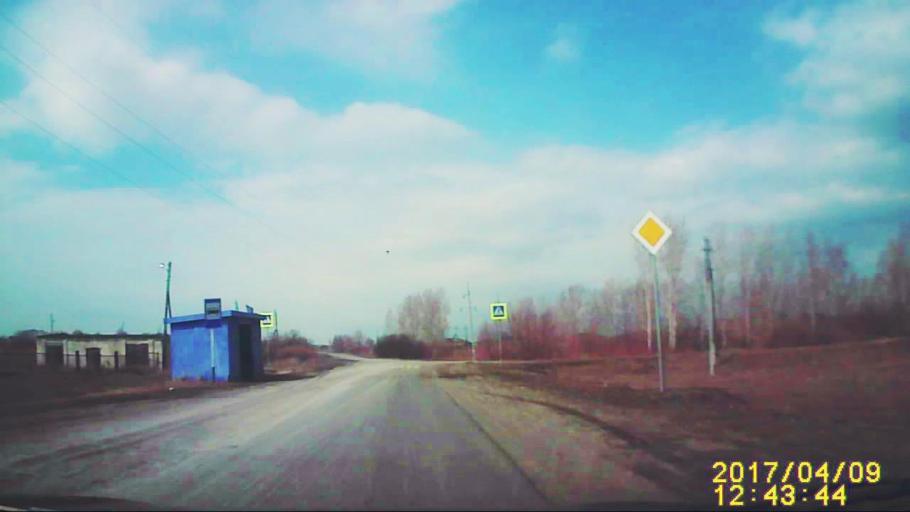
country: RU
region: Ulyanovsk
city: Ignatovka
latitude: 54.0089
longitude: 47.9162
